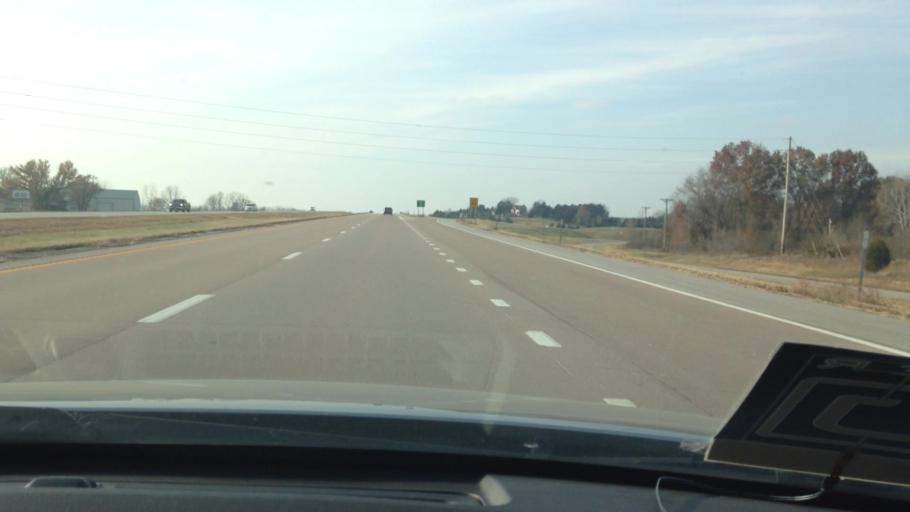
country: US
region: Missouri
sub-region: Cass County
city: Garden City
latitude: 38.4650
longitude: -93.9971
